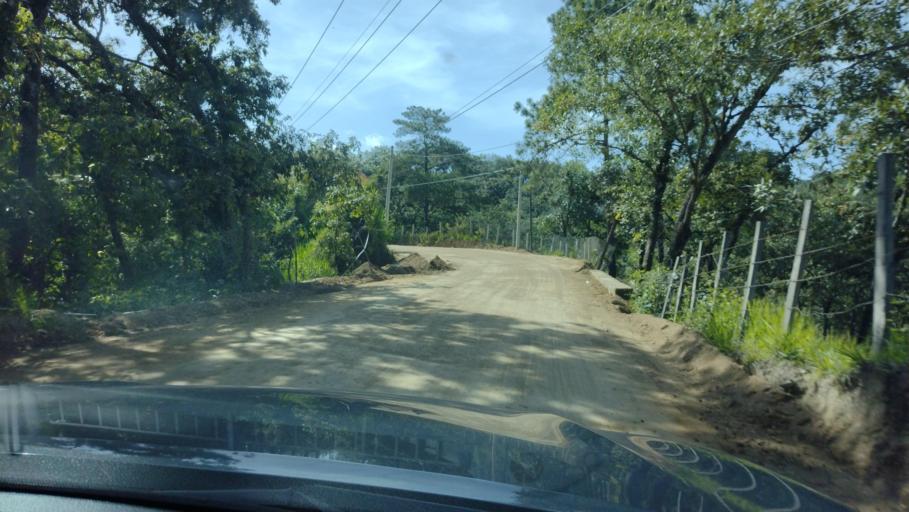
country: GT
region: Guatemala
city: Chinautla
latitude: 14.7617
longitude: -90.5243
